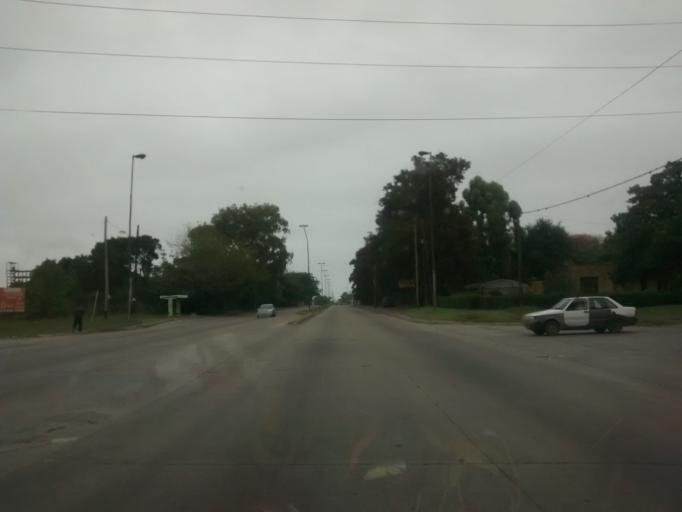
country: AR
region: Buenos Aires
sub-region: Partido de La Plata
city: La Plata
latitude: -34.9783
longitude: -58.0296
